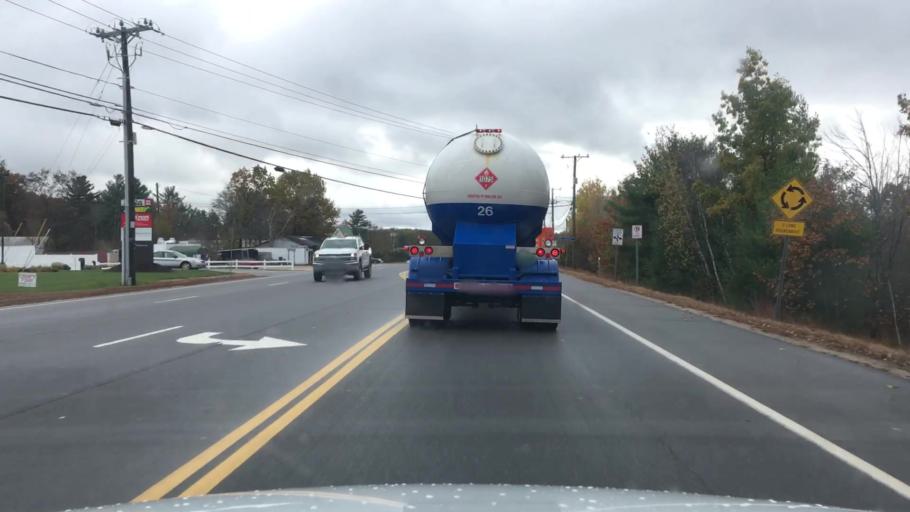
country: US
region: New Hampshire
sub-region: Strafford County
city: Lee
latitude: 43.1527
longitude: -71.0056
